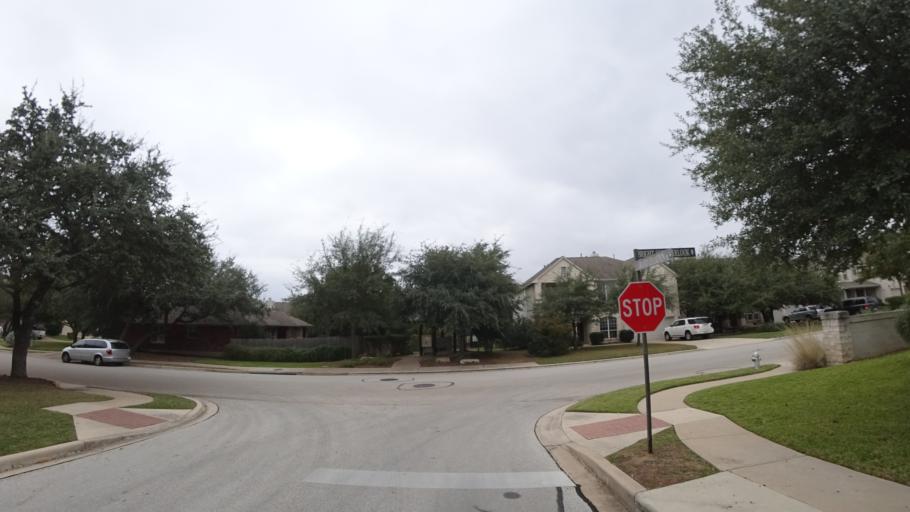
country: US
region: Texas
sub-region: Travis County
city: Bee Cave
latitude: 30.3555
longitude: -97.9077
